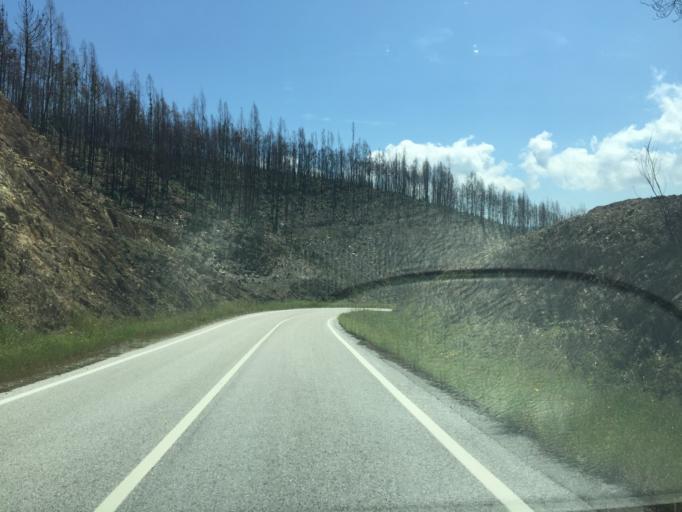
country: PT
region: Coimbra
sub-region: Pampilhosa da Serra
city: Pampilhosa da Serra
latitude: 39.9933
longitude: -7.9727
